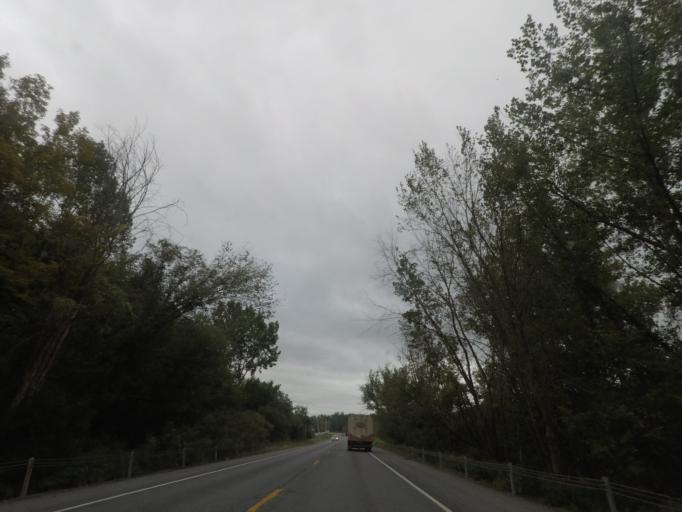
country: US
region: New York
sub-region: Rensselaer County
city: Hoosick Falls
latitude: 42.9385
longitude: -73.3652
